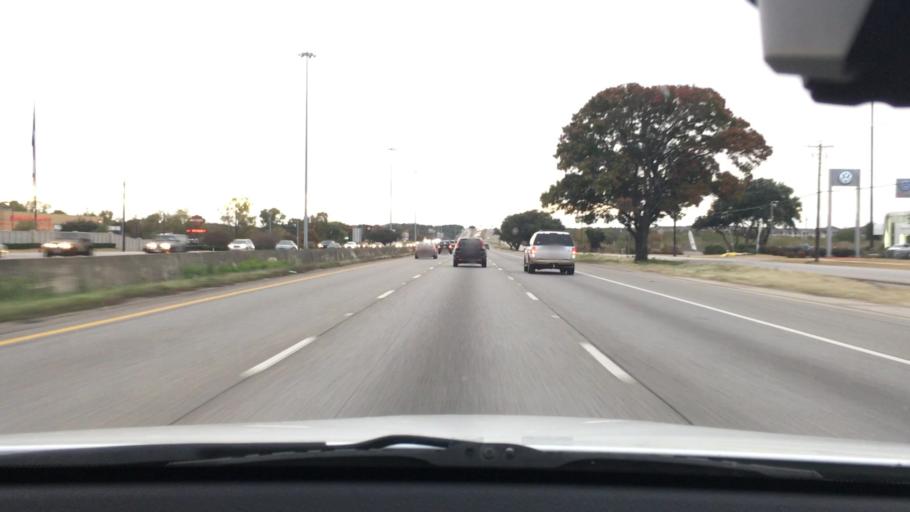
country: US
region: Texas
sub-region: Travis County
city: Onion Creek
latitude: 30.1457
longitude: -97.7942
